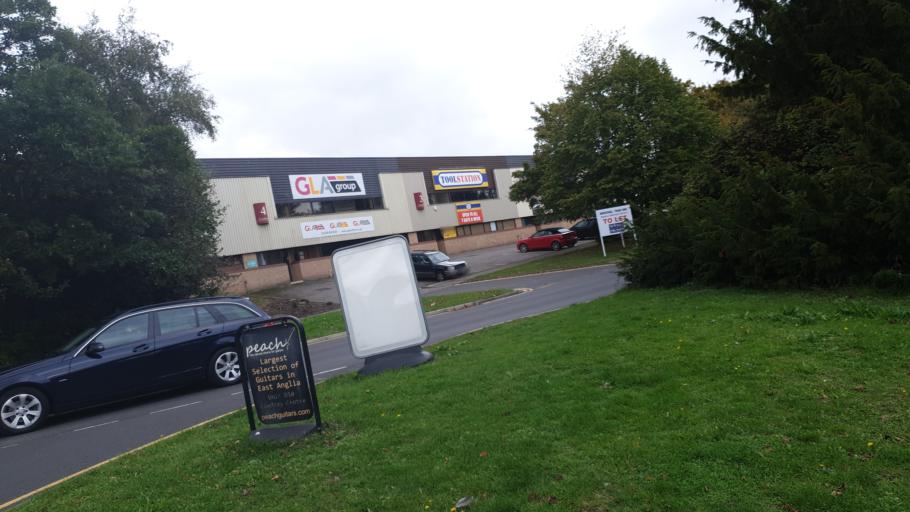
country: GB
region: England
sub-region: Essex
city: Colchester
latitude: 51.9191
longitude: 0.9296
